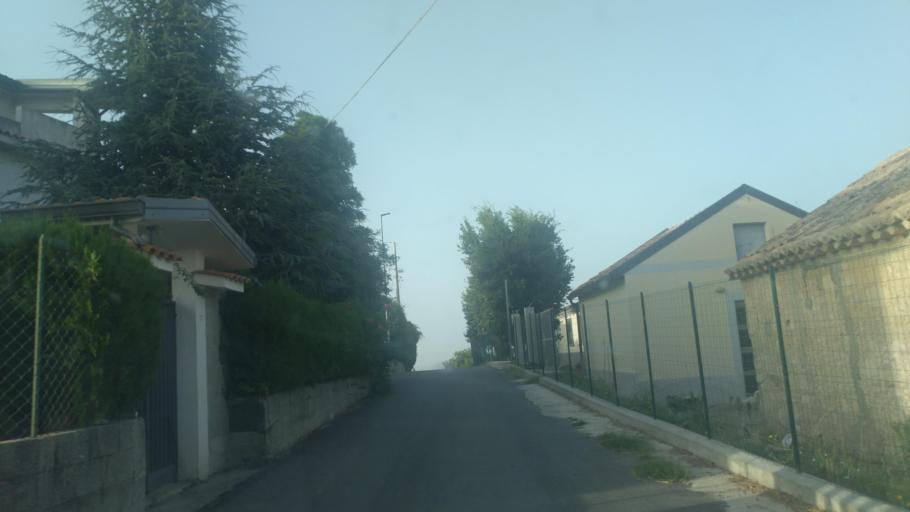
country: IT
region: Calabria
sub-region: Provincia di Catanzaro
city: Staletti
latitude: 38.7646
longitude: 16.5328
